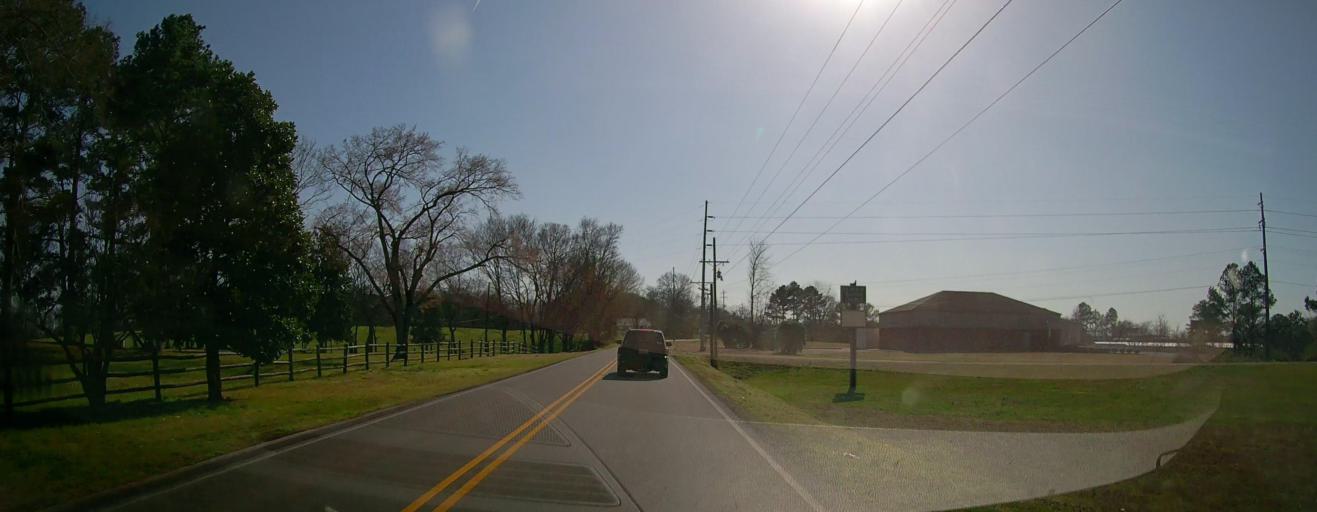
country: US
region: Alabama
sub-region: Lauderdale County
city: East Florence
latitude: 34.8318
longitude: -87.6138
